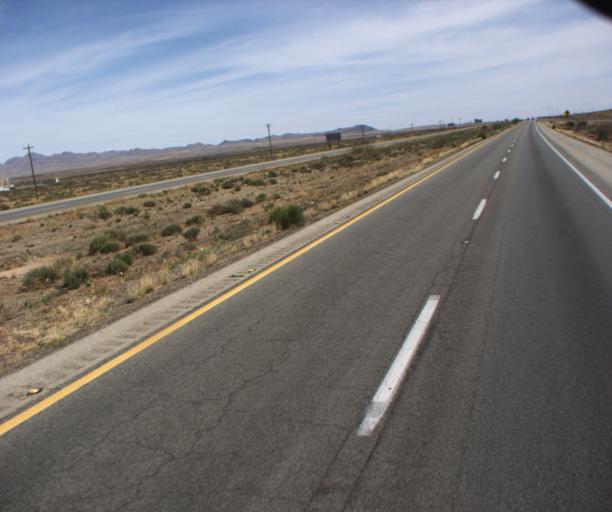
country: US
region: Arizona
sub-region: Cochise County
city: Willcox
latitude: 32.3141
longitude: -109.7884
